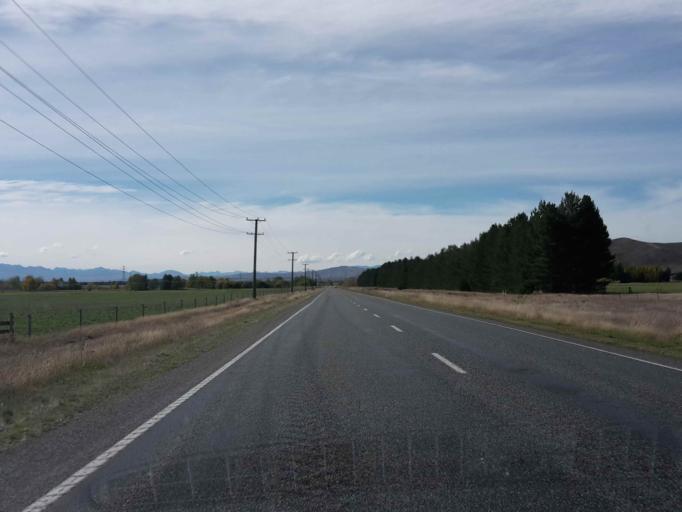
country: NZ
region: Otago
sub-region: Queenstown-Lakes District
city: Wanaka
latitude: -44.3108
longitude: 170.0577
